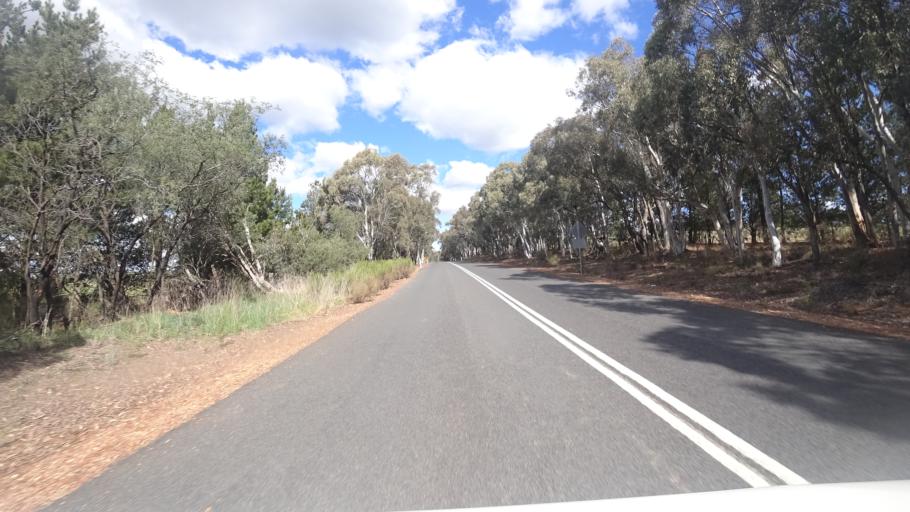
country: AU
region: New South Wales
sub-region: Oberon
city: Oberon
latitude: -33.6707
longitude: 149.7829
